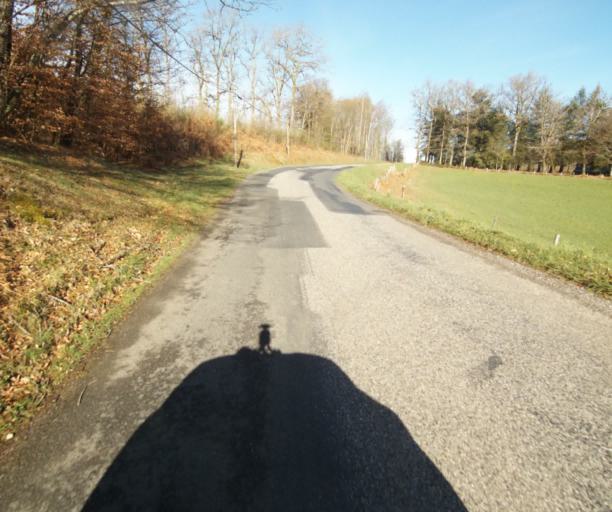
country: FR
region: Limousin
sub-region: Departement de la Correze
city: Laguenne
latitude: 45.2706
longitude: 1.8671
